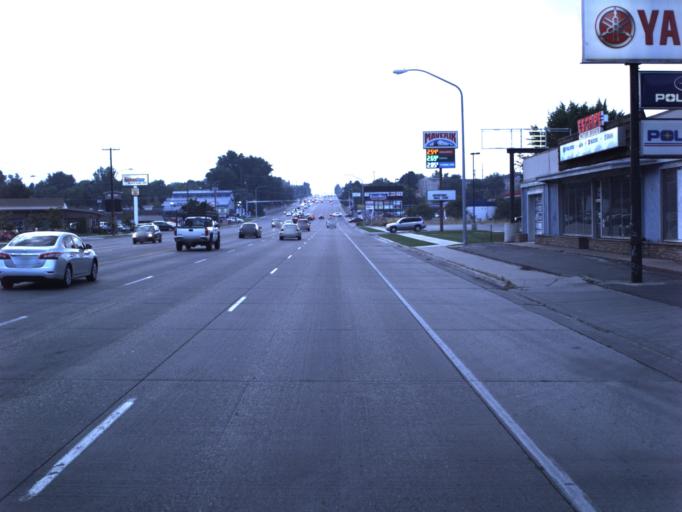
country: US
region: Utah
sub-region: Utah County
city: Provo
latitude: 40.2539
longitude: -111.6700
